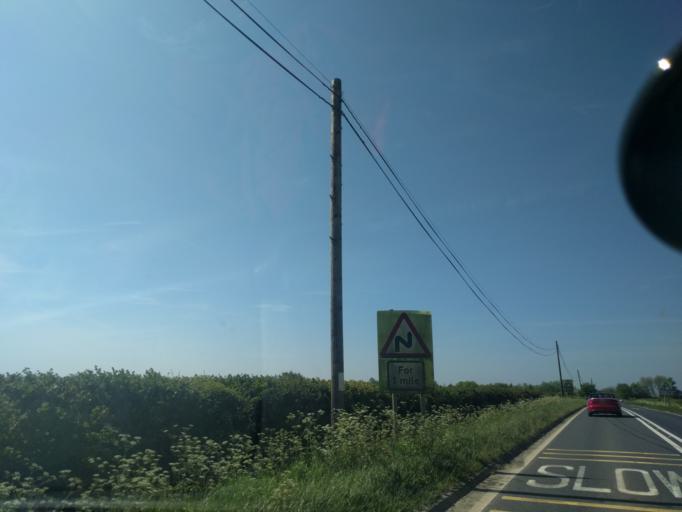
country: GB
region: England
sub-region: Somerset
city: Ilchester
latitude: 51.0604
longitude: -2.6357
